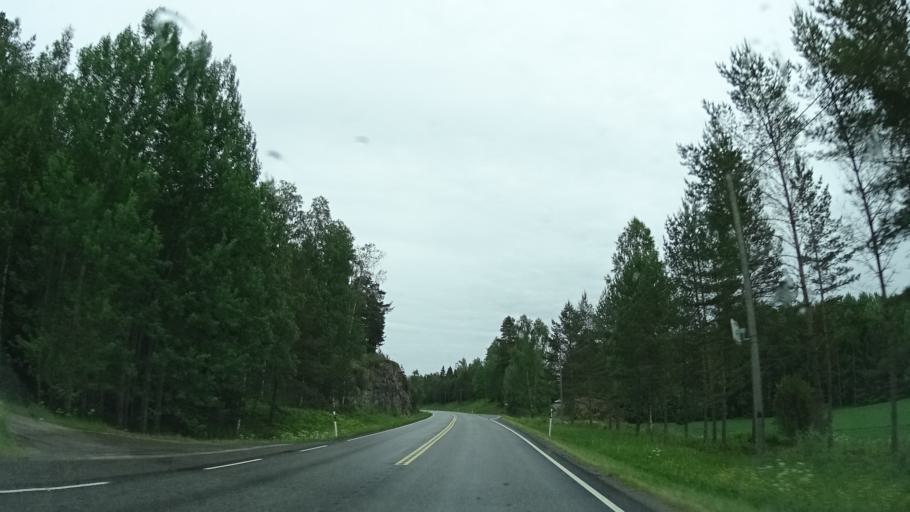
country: FI
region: Varsinais-Suomi
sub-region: Salo
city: Pernioe
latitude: 60.0842
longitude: 23.2328
